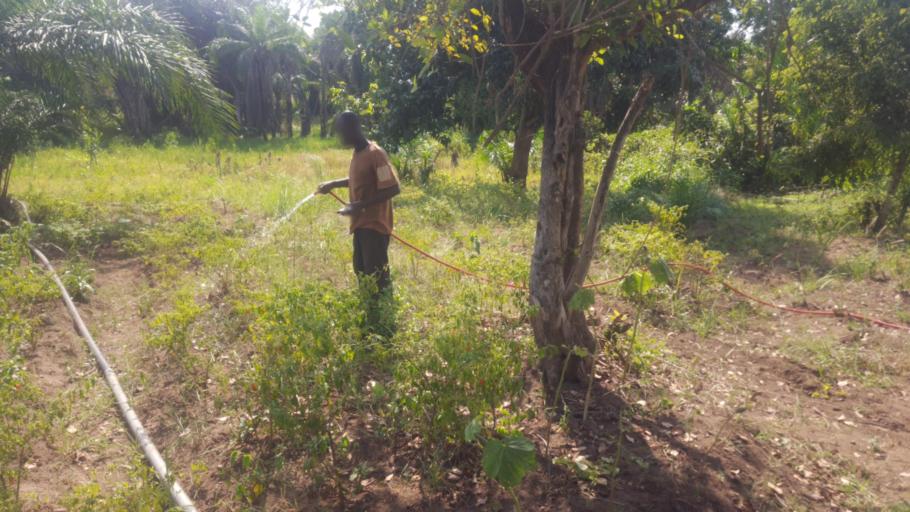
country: TG
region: Centrale
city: Sotouboua
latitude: 8.1364
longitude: 0.9392
